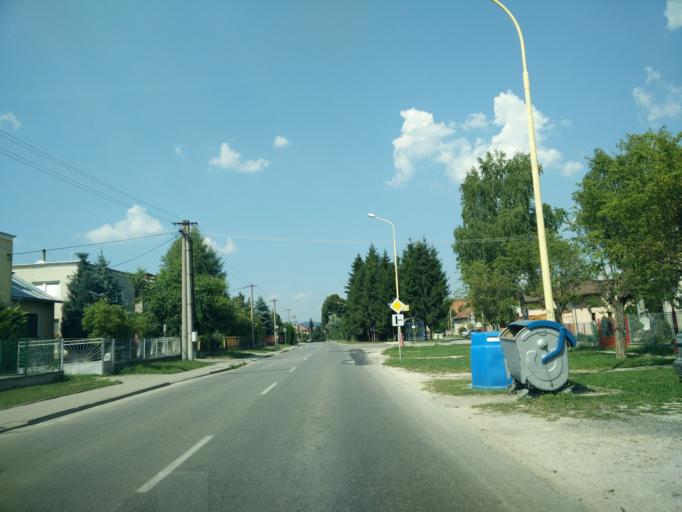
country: SK
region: Zilinsky
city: Rajec
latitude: 49.0807
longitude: 18.6324
